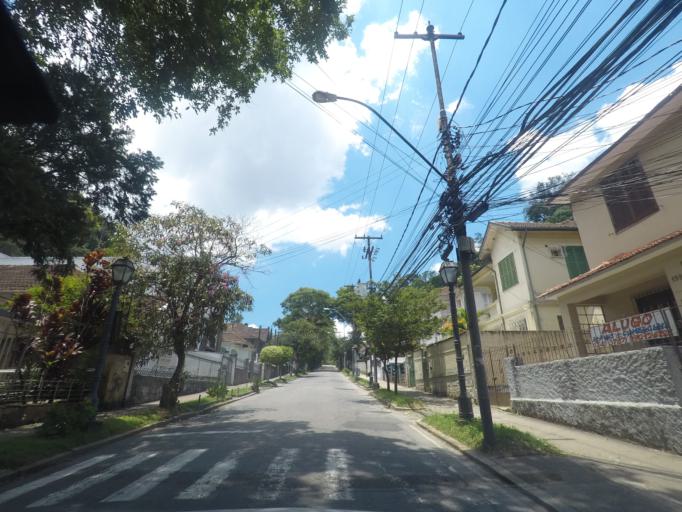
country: BR
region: Rio de Janeiro
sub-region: Petropolis
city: Petropolis
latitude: -22.5068
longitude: -43.1735
